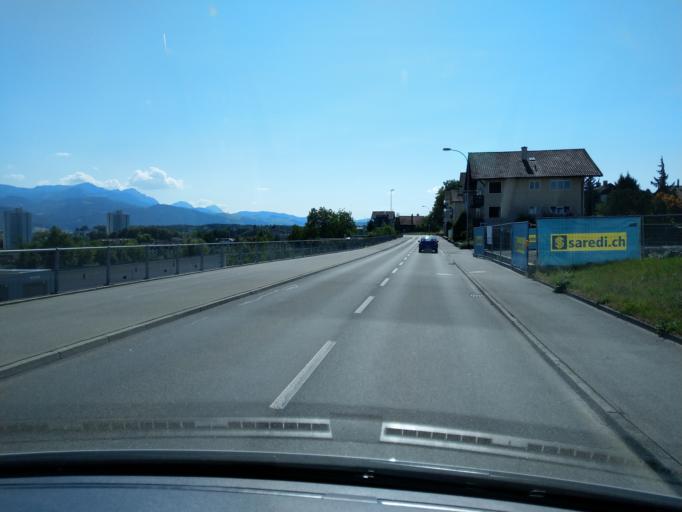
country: CH
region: Lucerne
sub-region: Hochdorf District
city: Emmen
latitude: 47.0997
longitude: 8.2815
